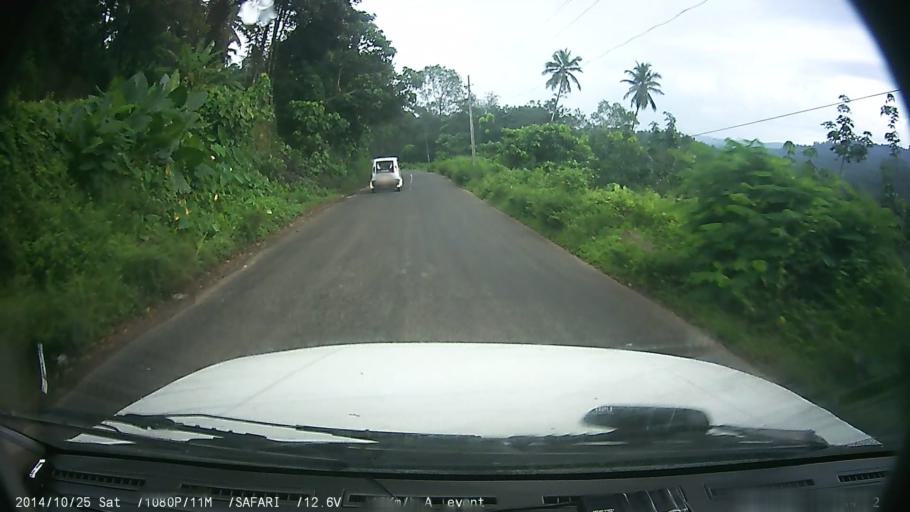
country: IN
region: Kerala
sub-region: Ernakulam
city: Muvattupuzha
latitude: 9.9251
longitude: 76.5814
